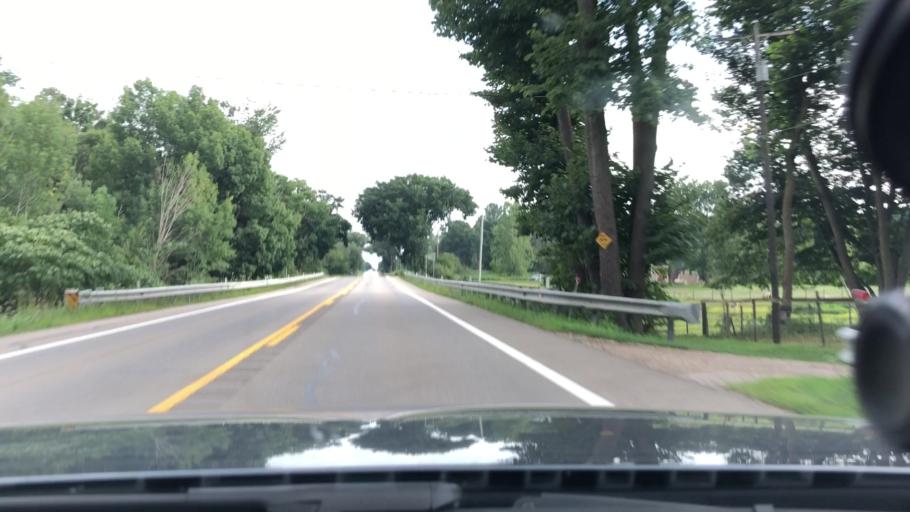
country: US
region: Michigan
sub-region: Washtenaw County
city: Manchester
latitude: 42.2174
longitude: -84.0334
